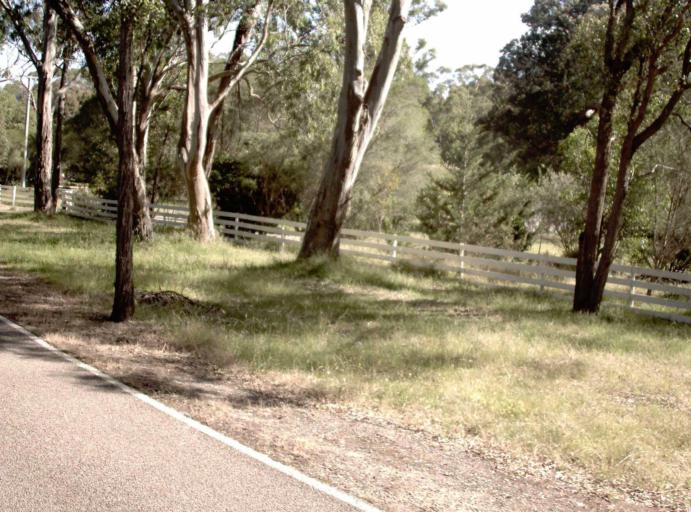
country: AU
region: Victoria
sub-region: East Gippsland
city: Lakes Entrance
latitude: -37.7853
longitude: 147.8280
